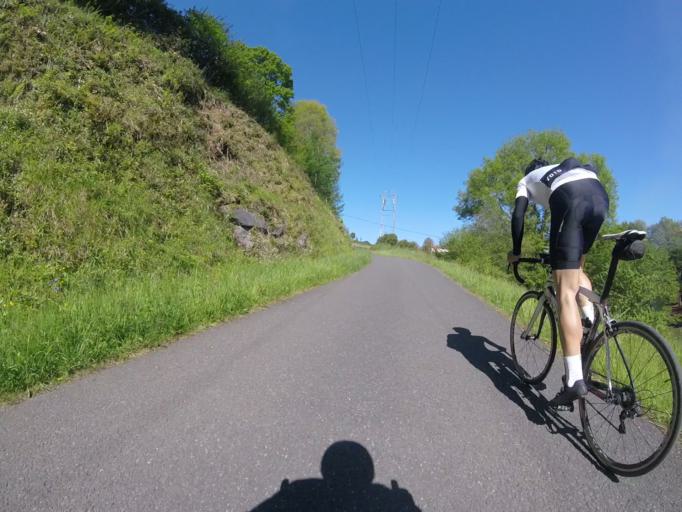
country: ES
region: Basque Country
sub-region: Provincia de Guipuzcoa
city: Errezil
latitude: 43.1704
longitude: -2.2020
